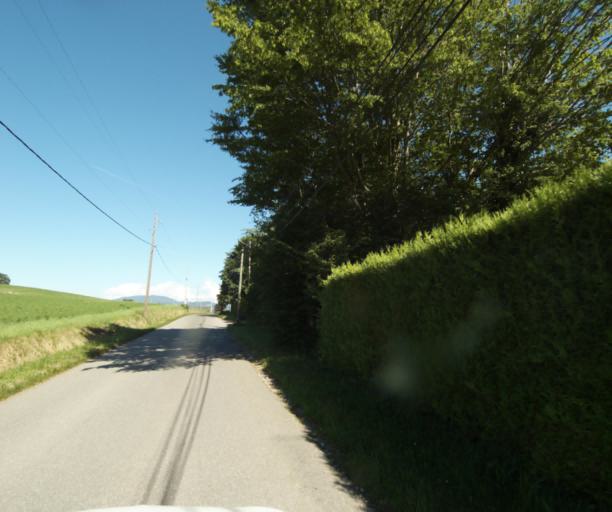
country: FR
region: Rhone-Alpes
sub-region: Departement de la Haute-Savoie
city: Ballaison
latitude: 46.2942
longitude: 6.3340
